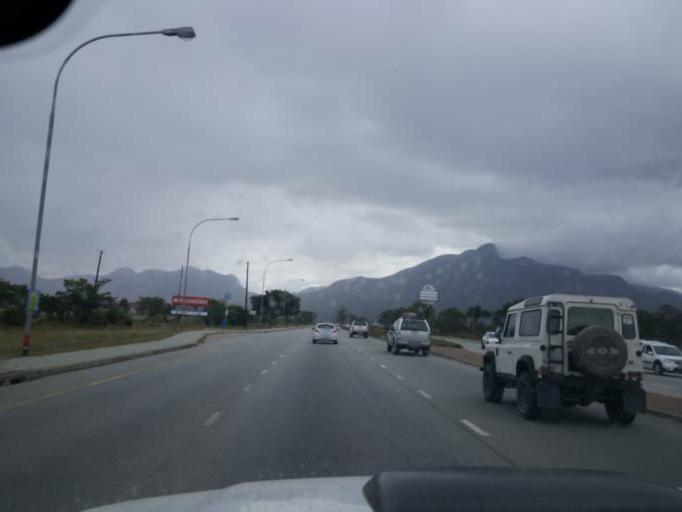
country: ZA
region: Western Cape
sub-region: Eden District Municipality
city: George
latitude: -33.9777
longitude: 22.4951
